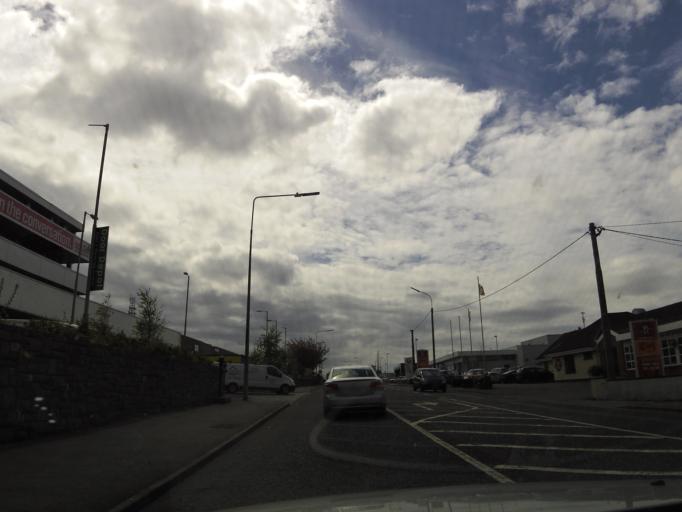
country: IE
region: Connaught
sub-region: County Galway
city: Gaillimh
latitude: 53.2942
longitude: -9.0165
